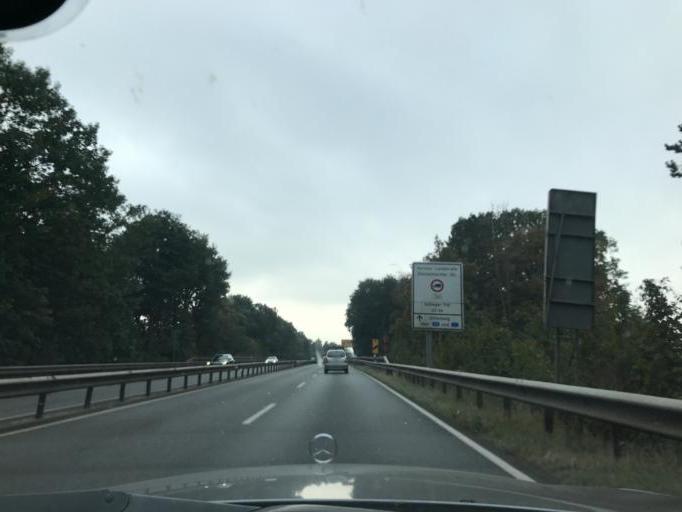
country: DE
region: Lower Saxony
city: Delmenhorst
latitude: 53.0390
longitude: 8.6812
